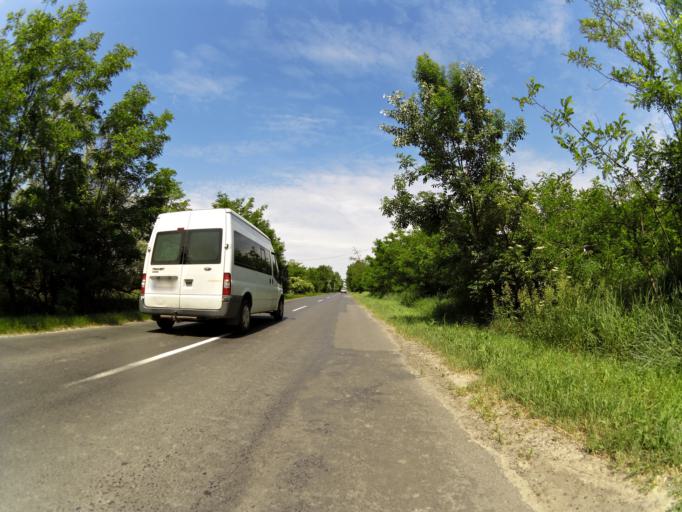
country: HU
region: Csongrad
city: Opusztaszer
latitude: 46.4717
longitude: 20.0905
